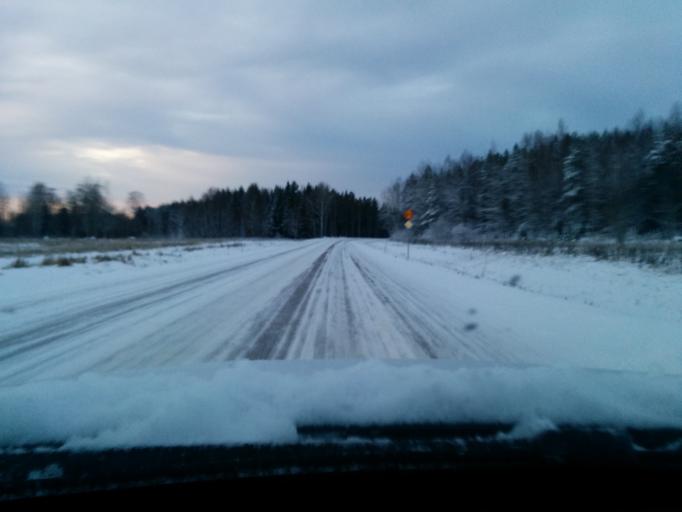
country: SE
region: Uppsala
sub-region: Tierps Kommun
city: Orbyhus
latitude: 60.1730
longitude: 17.5834
